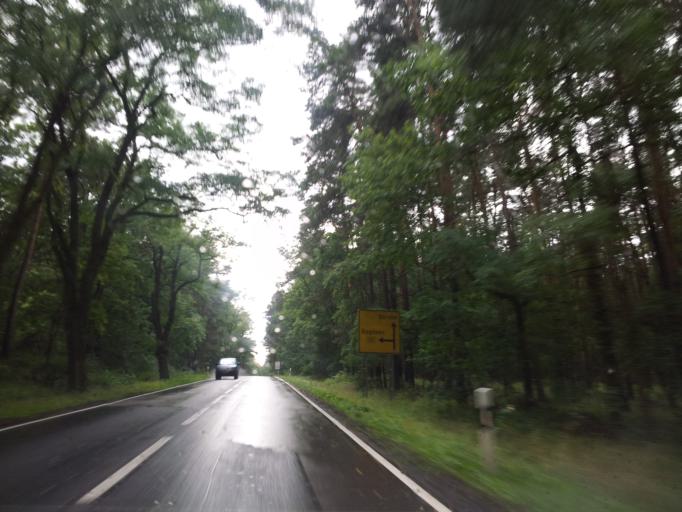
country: DE
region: Brandenburg
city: Graben
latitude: 52.2589
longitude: 12.4445
